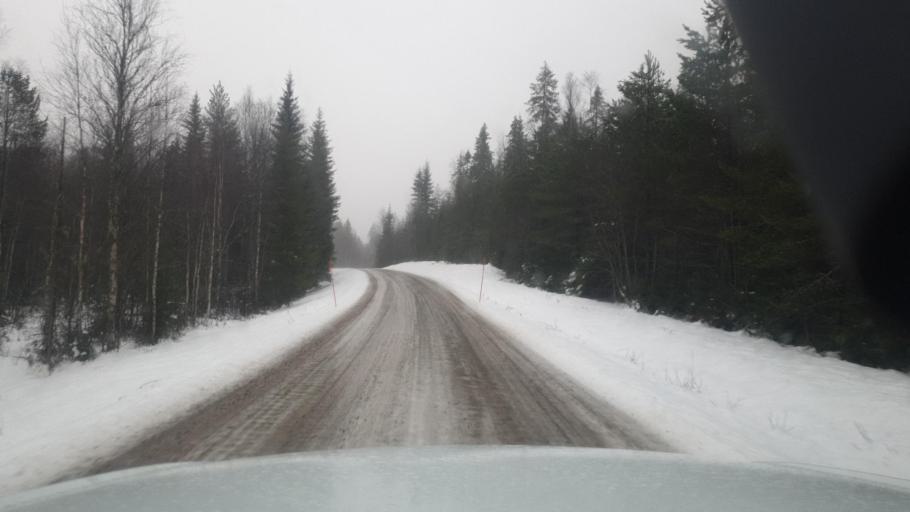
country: SE
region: Vaermland
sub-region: Eda Kommun
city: Charlottenberg
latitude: 60.0549
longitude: 12.5601
